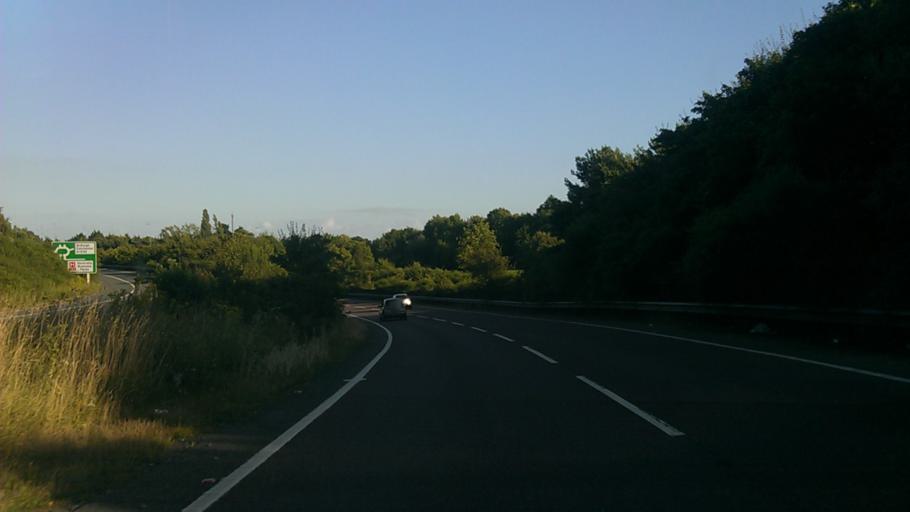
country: GB
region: England
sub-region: Essex
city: Colchester
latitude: 51.9237
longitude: 0.9311
